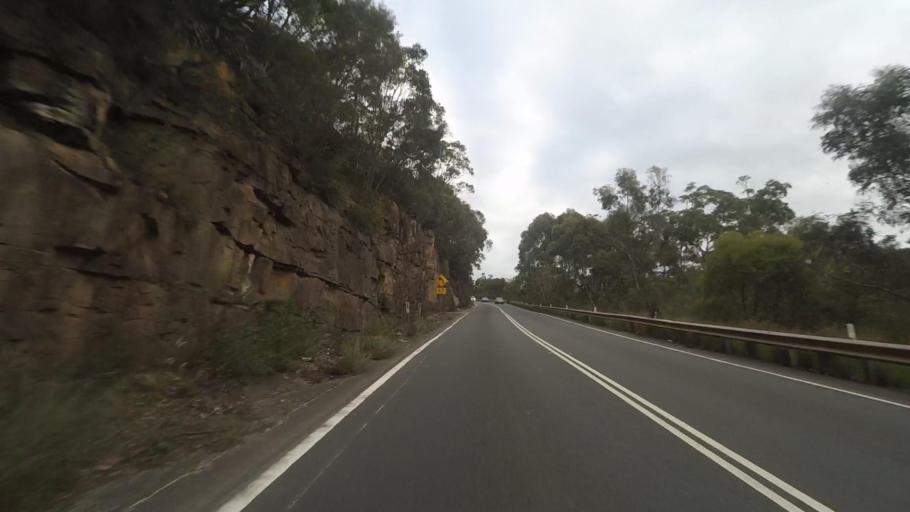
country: AU
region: New South Wales
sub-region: Sutherland Shire
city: Engadine
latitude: -34.0703
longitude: 150.9983
